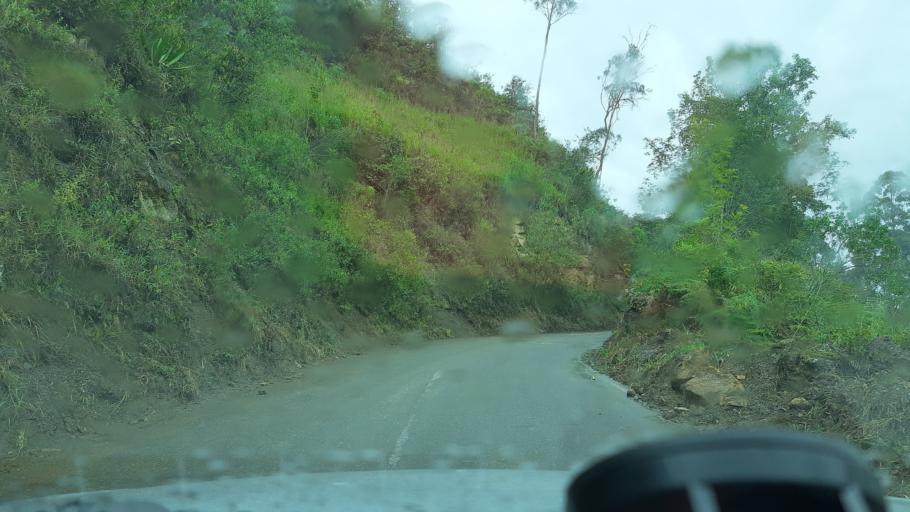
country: CO
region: Boyaca
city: Chinavita
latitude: 5.1699
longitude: -73.3816
